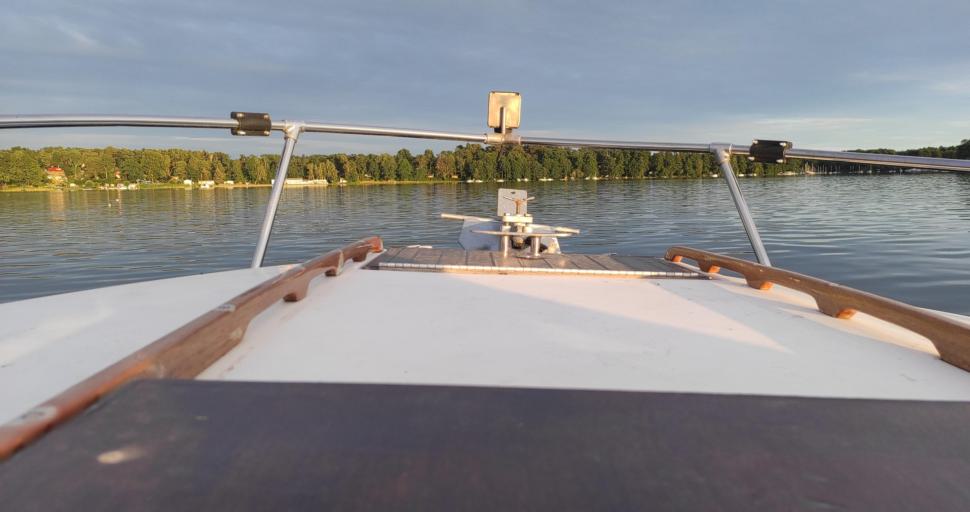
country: DE
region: Brandenburg
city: Friedland
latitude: 52.0201
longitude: 14.1850
